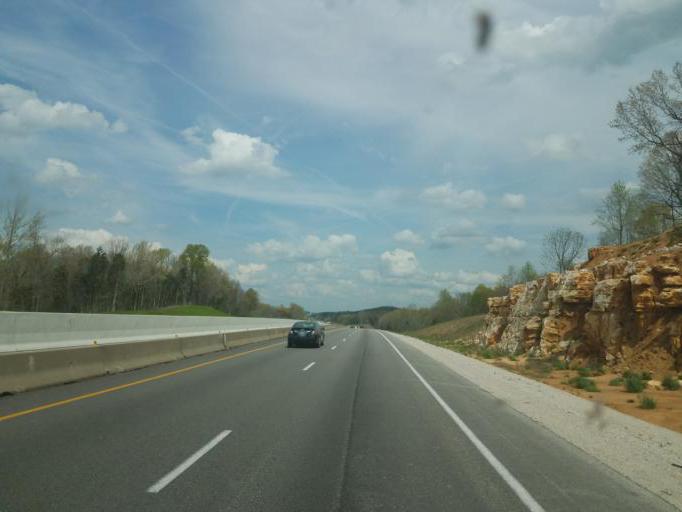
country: US
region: Kentucky
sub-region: Hart County
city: Munfordville
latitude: 37.4038
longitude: -85.8815
